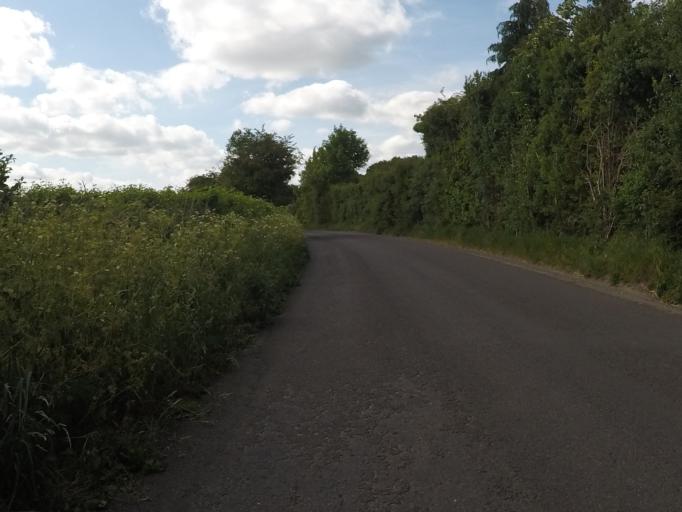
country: GB
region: England
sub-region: Oxfordshire
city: Witney
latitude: 51.8156
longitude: -1.5188
